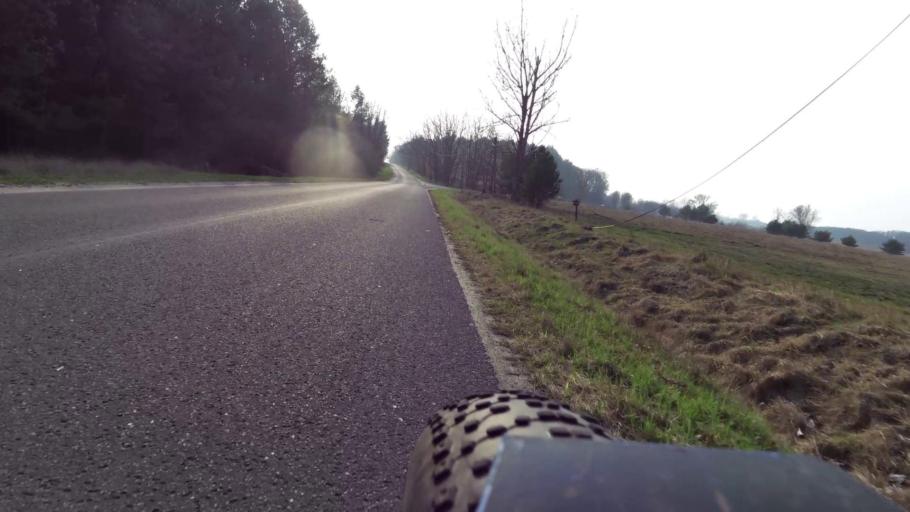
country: PL
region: Lubusz
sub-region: Powiat slubicki
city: Cybinka
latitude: 52.2476
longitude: 14.7281
